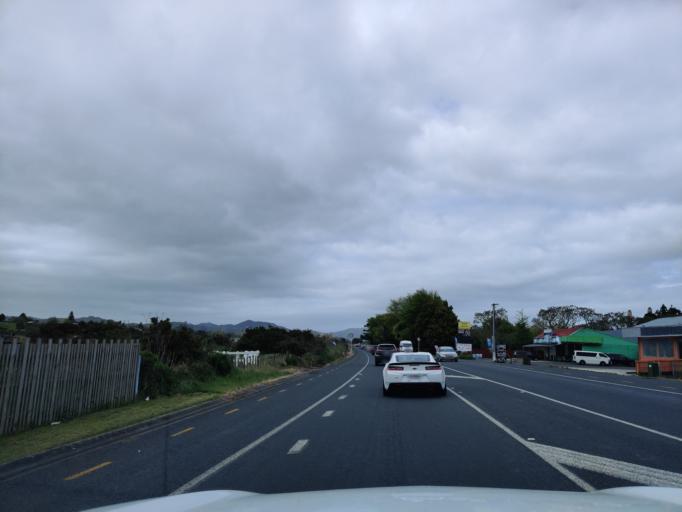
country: NZ
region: Waikato
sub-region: Waikato District
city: Te Kauwhata
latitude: -37.5288
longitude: 175.1593
